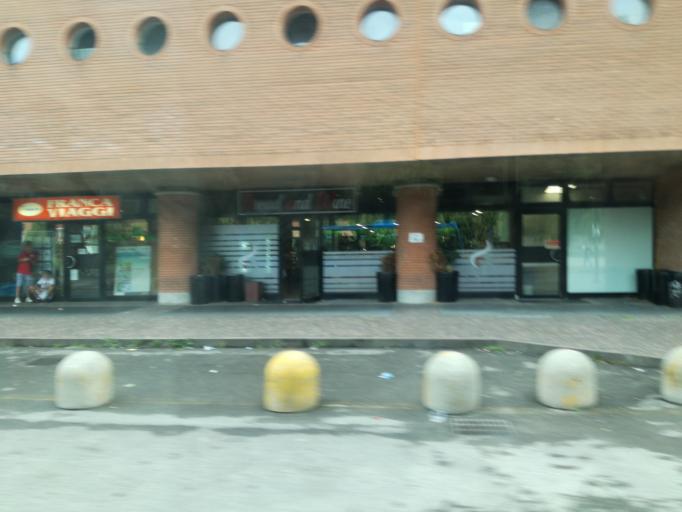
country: IT
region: Lombardy
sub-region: Provincia di Monza e Brianza
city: Vimercate
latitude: 45.6102
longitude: 9.3712
